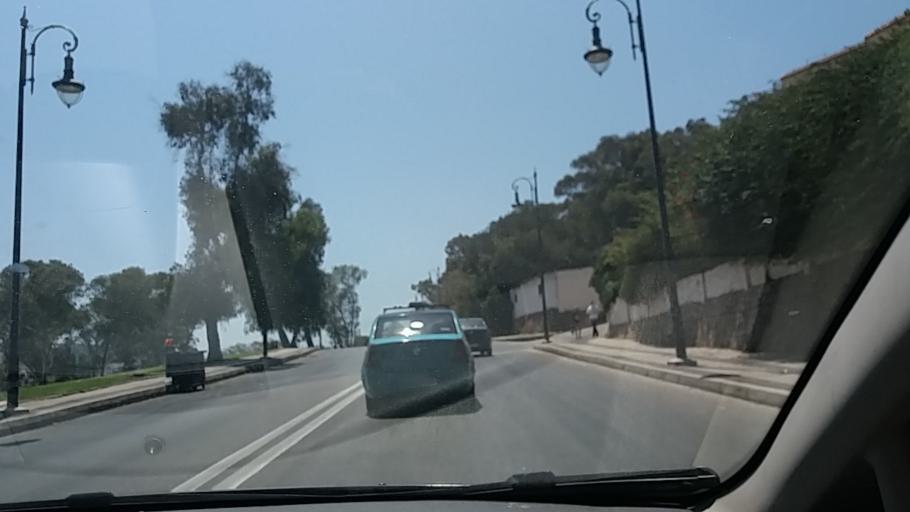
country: MA
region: Tanger-Tetouan
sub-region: Tanger-Assilah
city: Tangier
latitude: 35.7864
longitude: -5.8366
